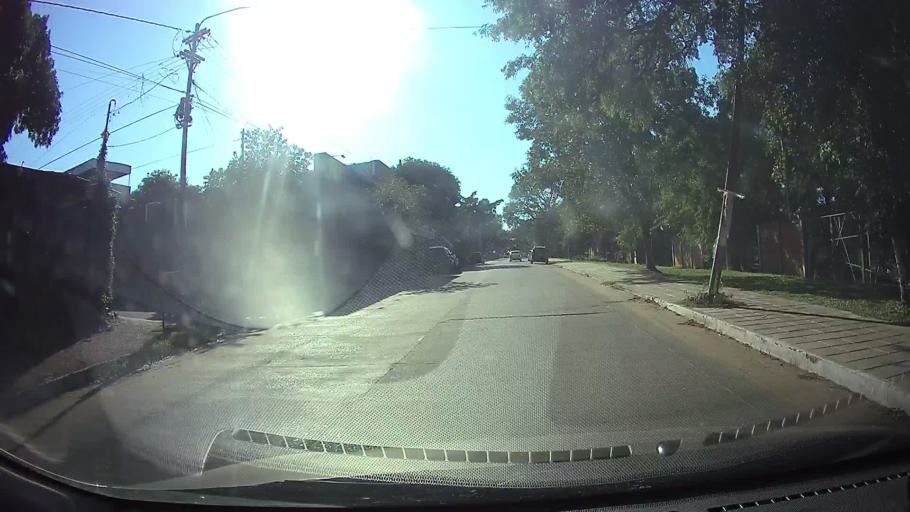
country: PY
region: Central
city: Villa Elisa
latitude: -25.3774
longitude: -57.5829
